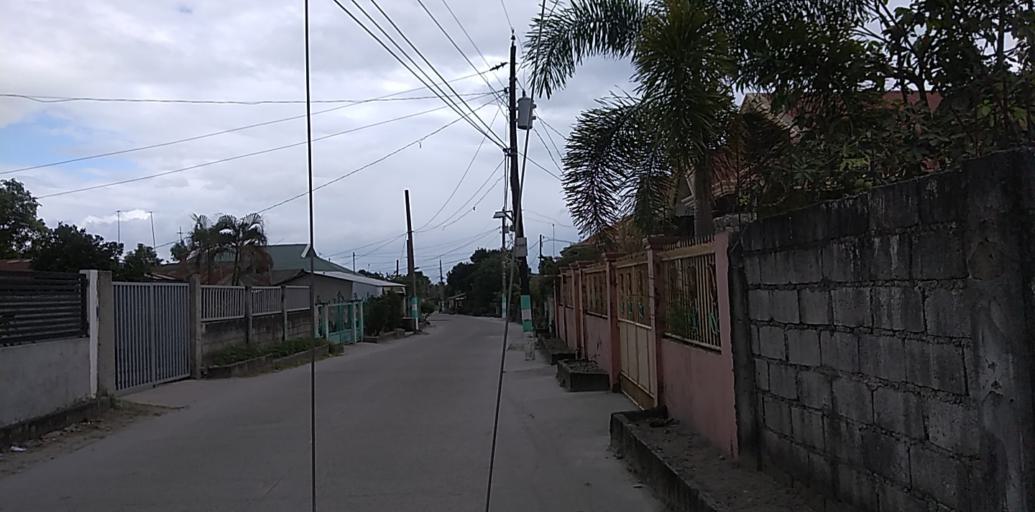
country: PH
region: Central Luzon
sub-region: Province of Pampanga
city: Pio
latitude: 15.0448
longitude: 120.5359
